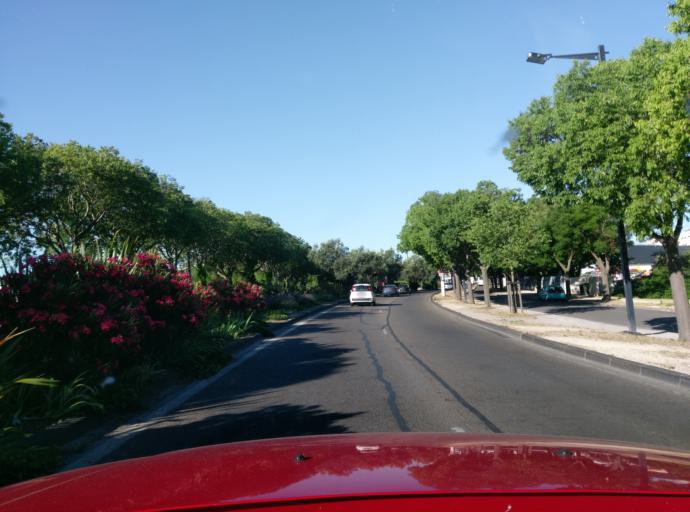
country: FR
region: Languedoc-Roussillon
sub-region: Departement du Gard
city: Nimes
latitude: 43.8340
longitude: 4.3868
